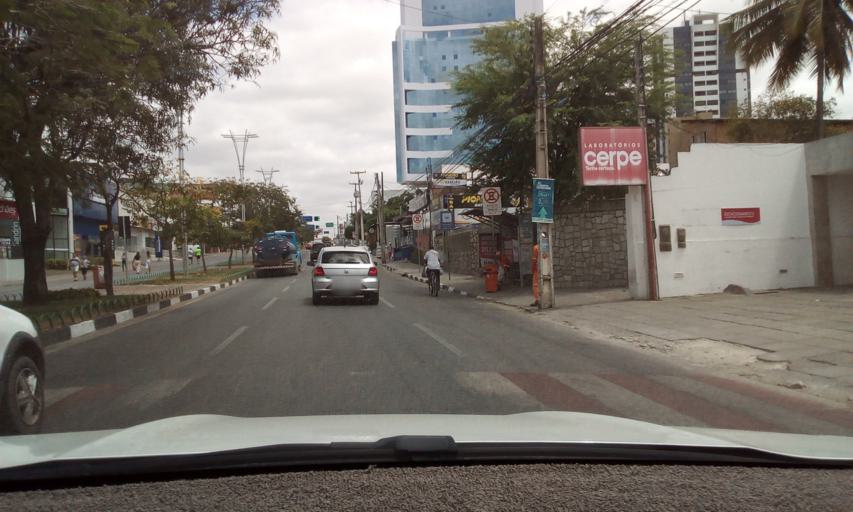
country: BR
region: Pernambuco
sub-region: Caruaru
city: Caruaru
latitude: -8.2718
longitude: -35.9750
